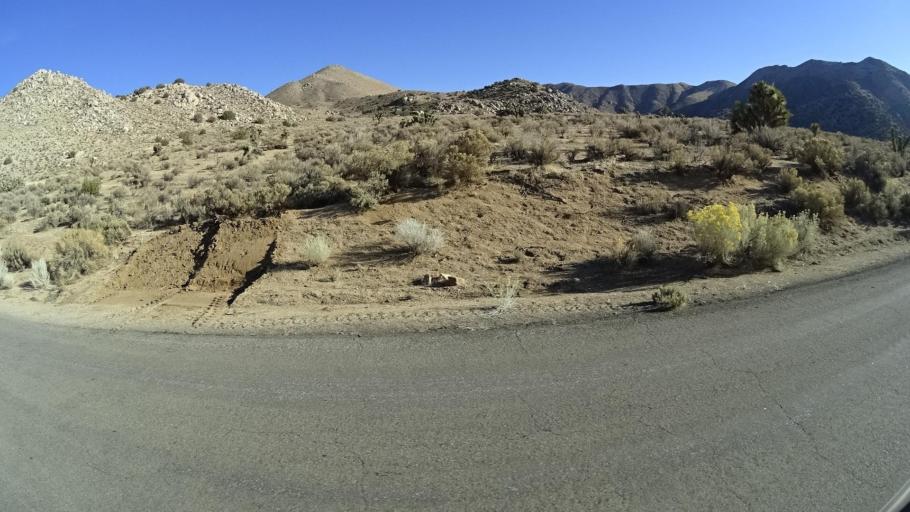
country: US
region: California
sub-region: Kern County
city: Weldon
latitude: 35.5897
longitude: -118.2410
